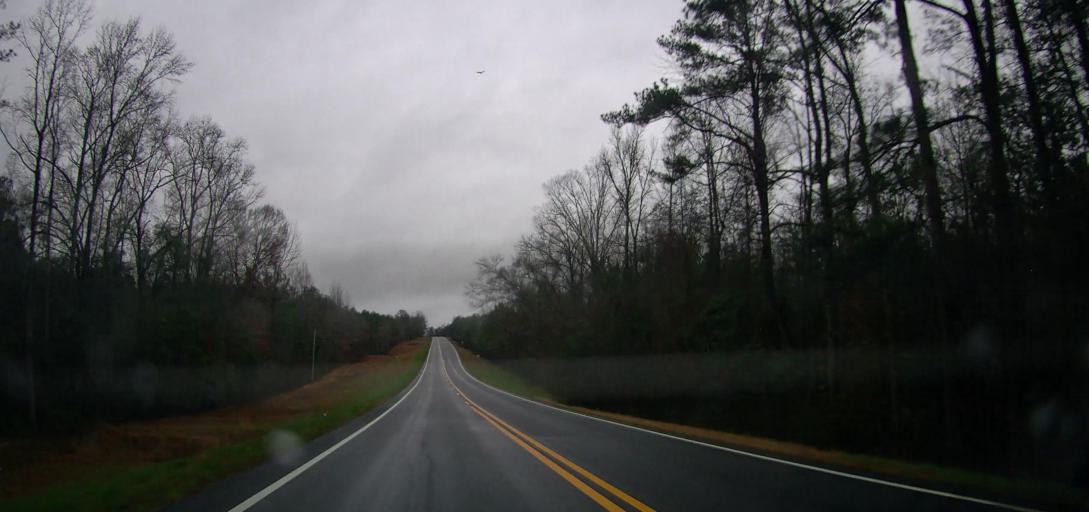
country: US
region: Alabama
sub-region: Bibb County
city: Centreville
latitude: 32.8236
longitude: -86.9445
